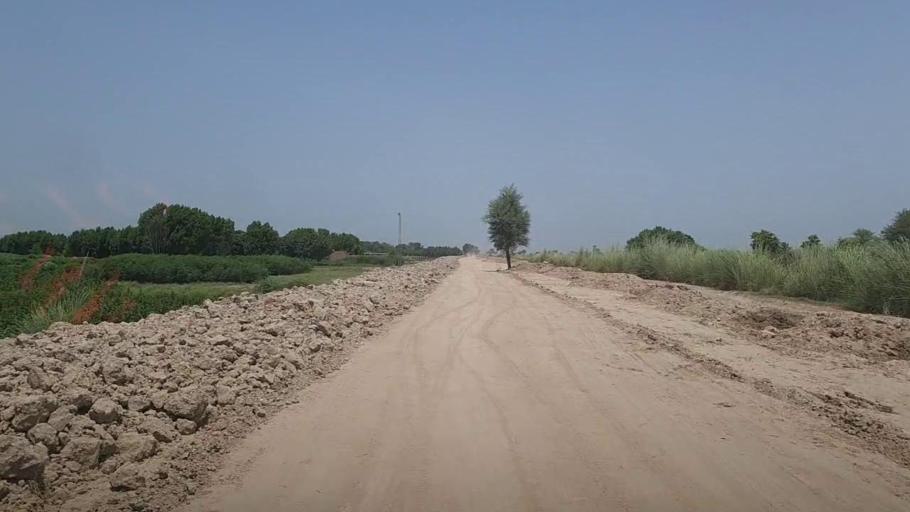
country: PK
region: Sindh
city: Pad Idan
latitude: 26.7862
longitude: 68.2773
